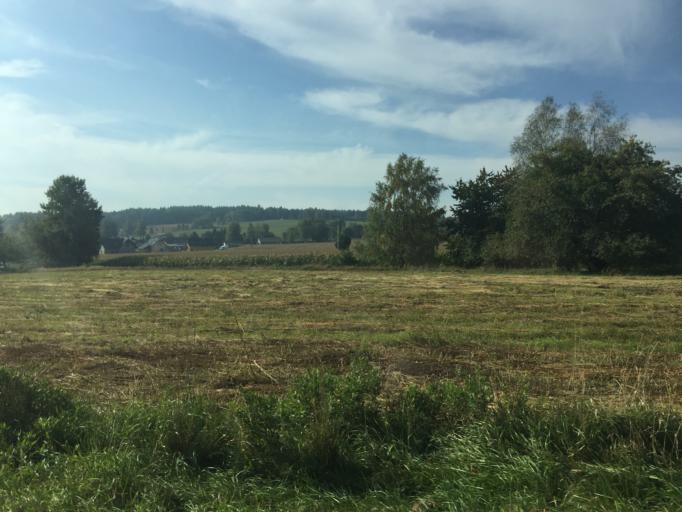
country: CZ
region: Ustecky
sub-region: Okres Decin
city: Decin
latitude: 50.8245
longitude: 14.2628
